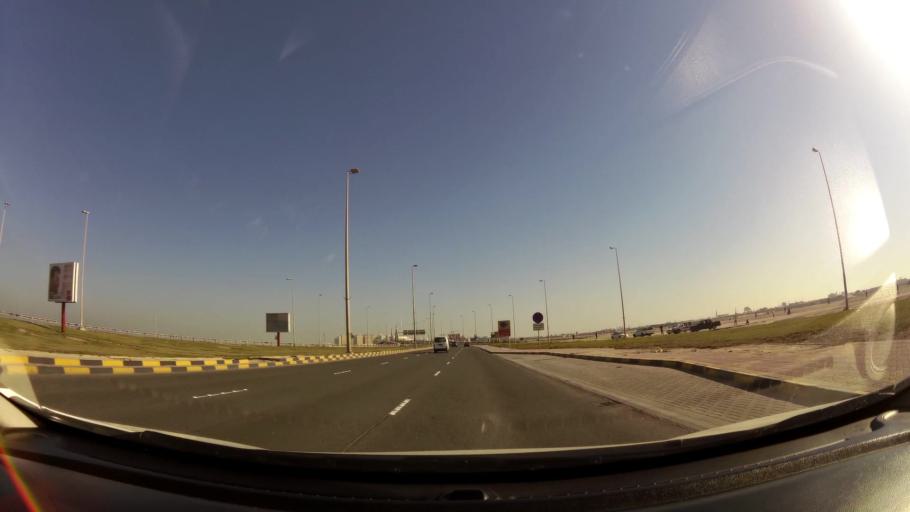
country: BH
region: Muharraq
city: Al Muharraq
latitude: 26.2478
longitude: 50.5912
